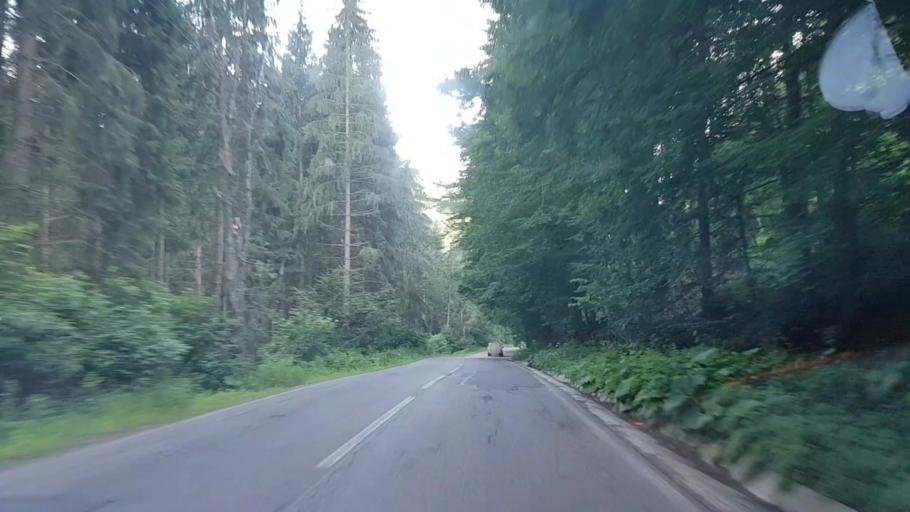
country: RO
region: Harghita
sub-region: Comuna Praid
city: Ocna de Sus
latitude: 46.5865
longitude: 25.2439
